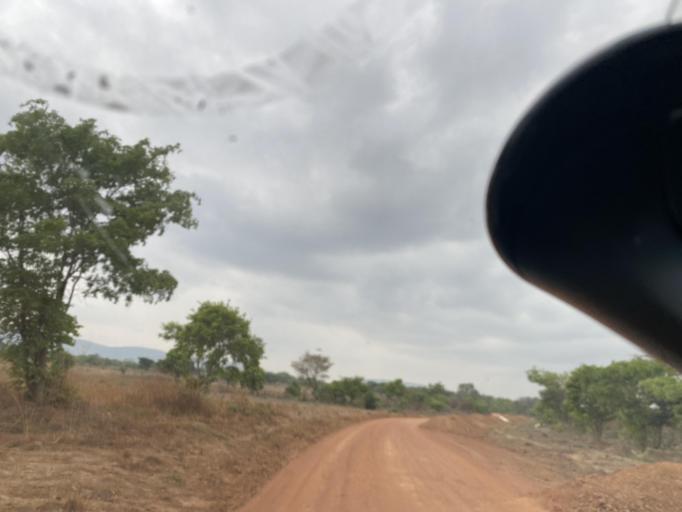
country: ZM
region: Lusaka
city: Chongwe
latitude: -15.2338
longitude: 28.7214
